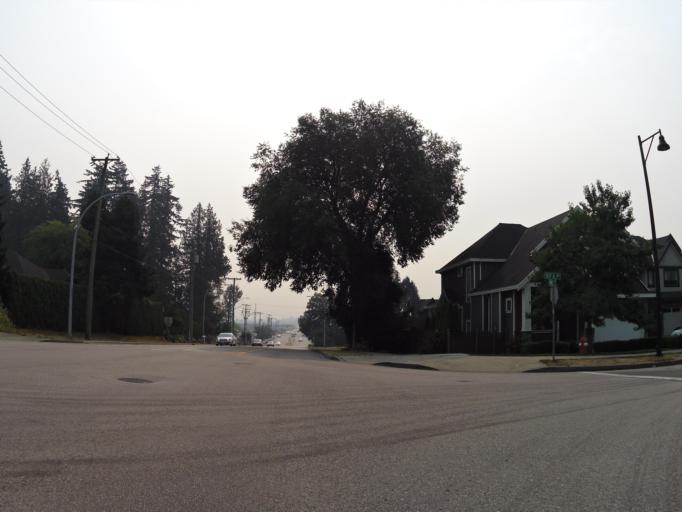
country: CA
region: British Columbia
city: Surrey
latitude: 49.1073
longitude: -122.7567
